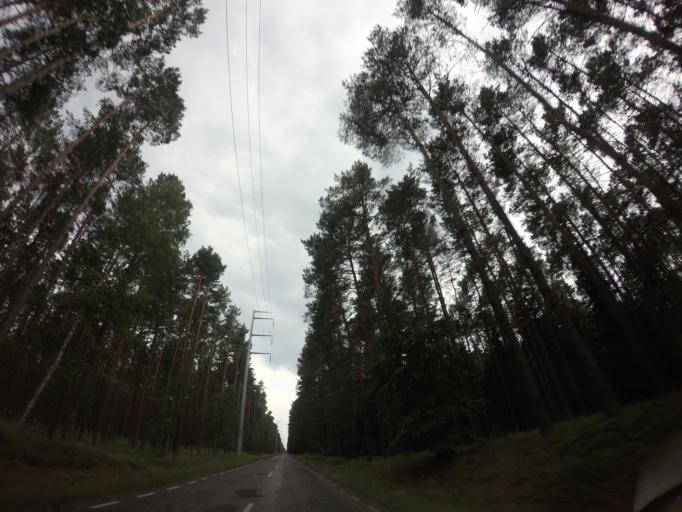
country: PL
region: West Pomeranian Voivodeship
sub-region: Powiat drawski
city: Czaplinek
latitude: 53.4716
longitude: 16.2233
